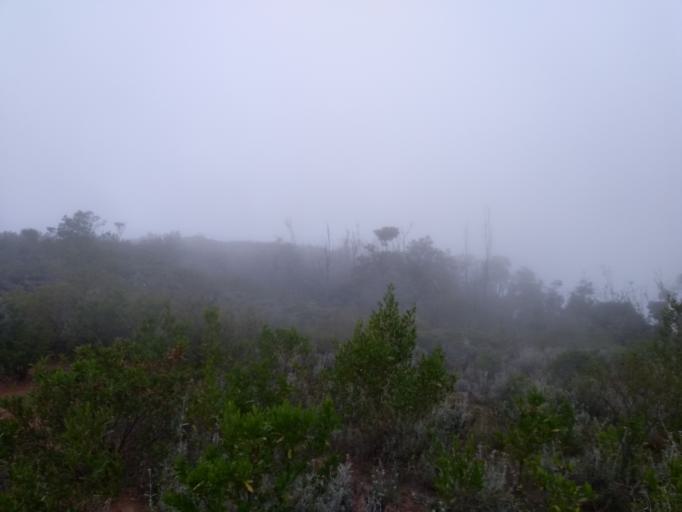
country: CO
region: Cesar
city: Manaure Balcon del Cesar
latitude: 10.2034
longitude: -73.0029
